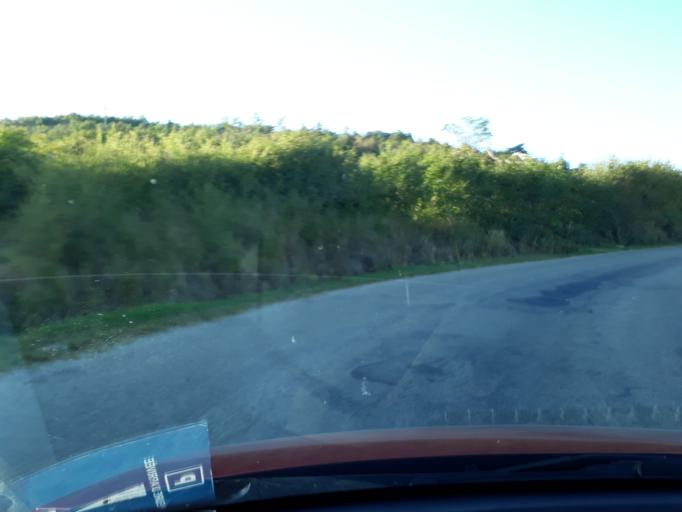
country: FR
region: Rhone-Alpes
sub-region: Departement de l'Ardeche
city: Felines
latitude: 45.3272
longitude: 4.7065
